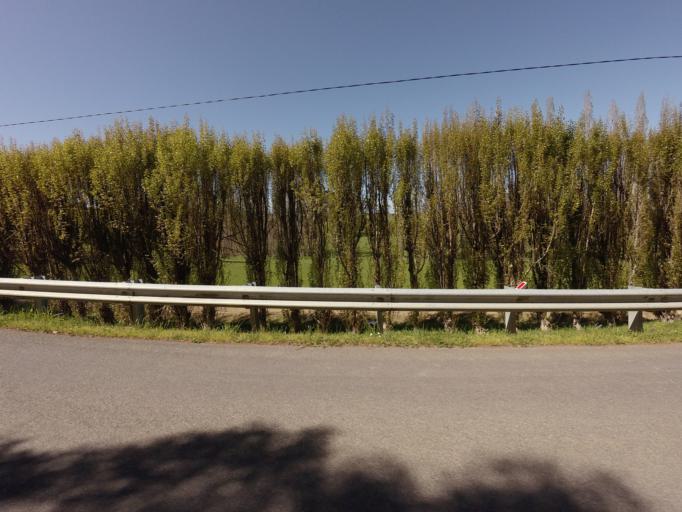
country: AU
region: Tasmania
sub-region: Derwent Valley
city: New Norfolk
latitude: -42.6722
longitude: 146.7891
